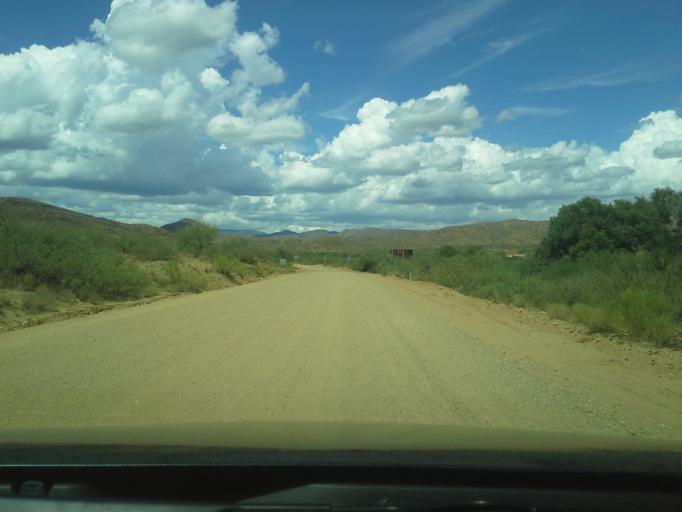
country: US
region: Arizona
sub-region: Yavapai County
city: Cordes Lakes
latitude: 34.2540
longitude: -112.1745
